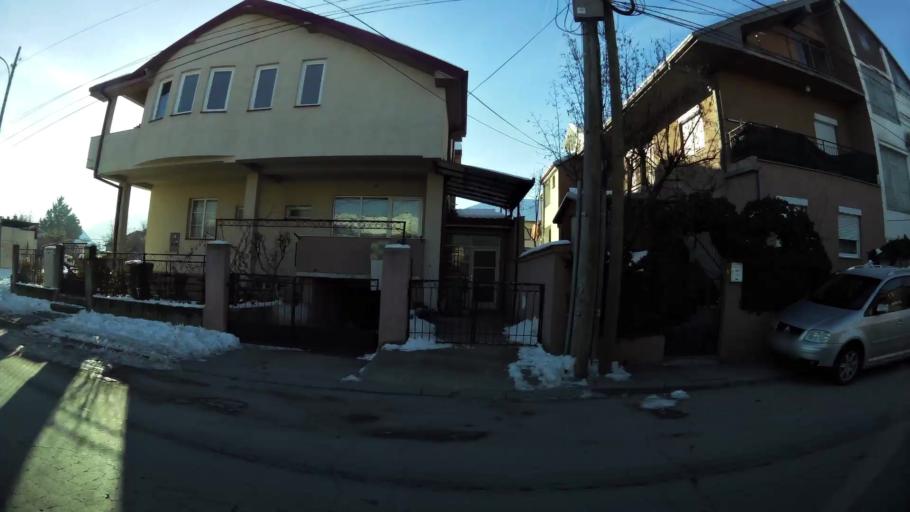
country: MK
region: Saraj
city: Saraj
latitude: 42.0084
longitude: 21.3431
